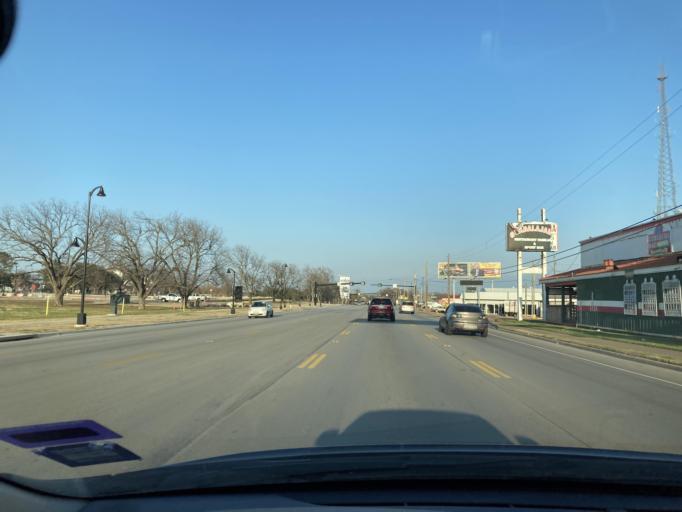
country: US
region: Texas
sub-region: Tarrant County
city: Arlington
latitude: 32.7395
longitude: -97.0953
